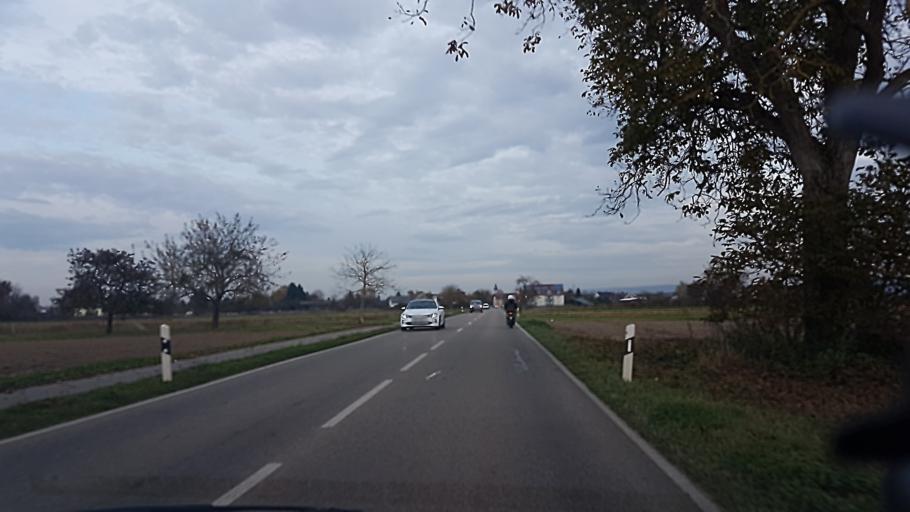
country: DE
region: Baden-Wuerttemberg
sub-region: Freiburg Region
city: Weisweil
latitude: 48.2196
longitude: 7.7044
